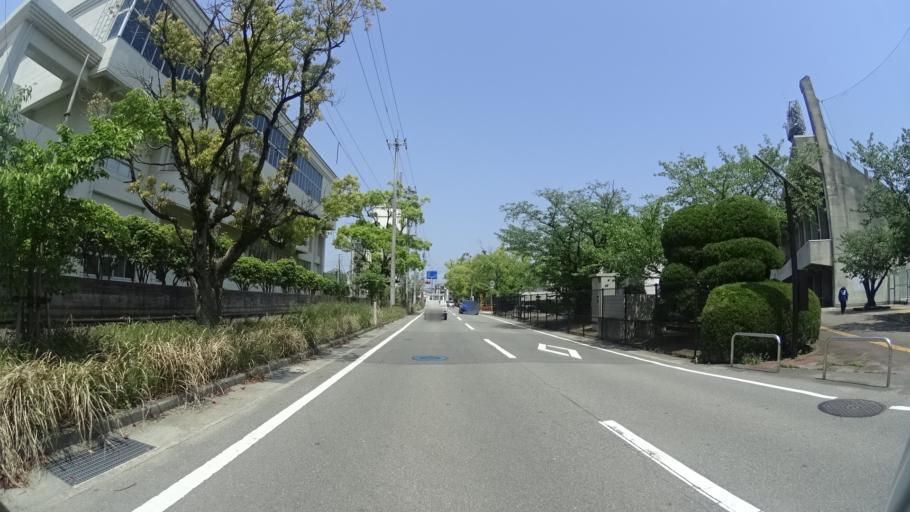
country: JP
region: Tokushima
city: Tokushima-shi
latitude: 34.0736
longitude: 134.5129
